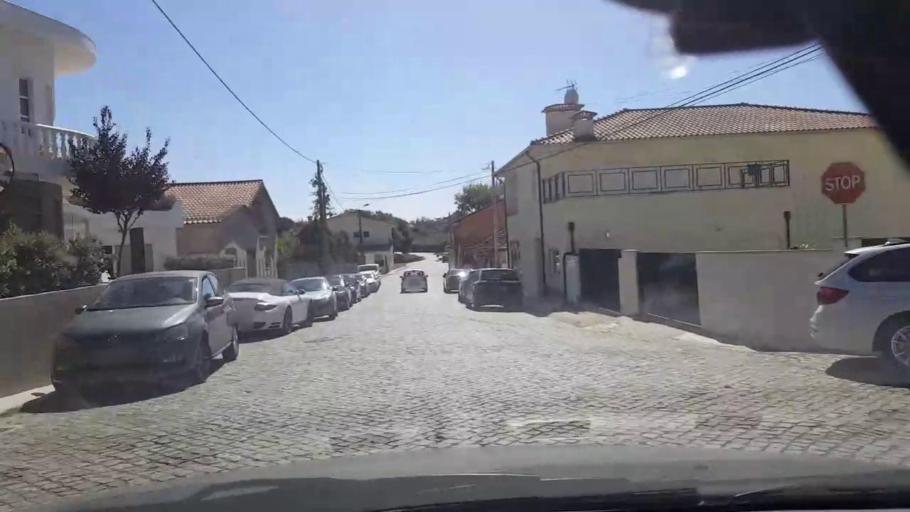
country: PT
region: Porto
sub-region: Vila do Conde
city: Arvore
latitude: 41.3199
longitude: -8.7235
